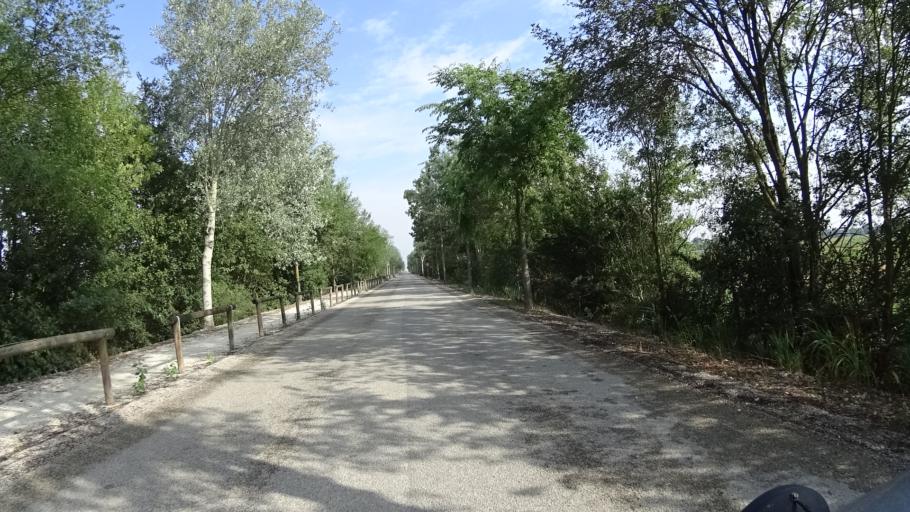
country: IT
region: Veneto
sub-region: Provincia di Venezia
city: Bibione
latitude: 45.6286
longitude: 12.9559
